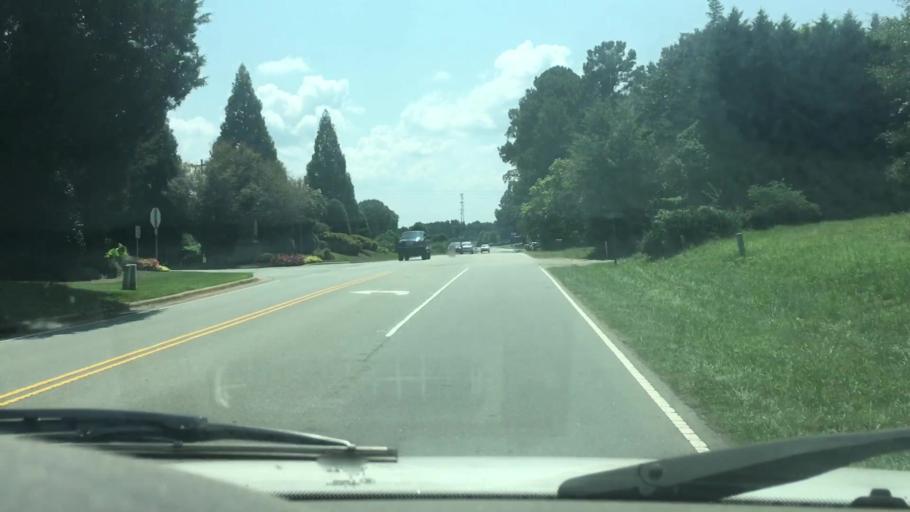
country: US
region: North Carolina
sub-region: Lincoln County
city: Westport
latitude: 35.4916
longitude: -80.9952
